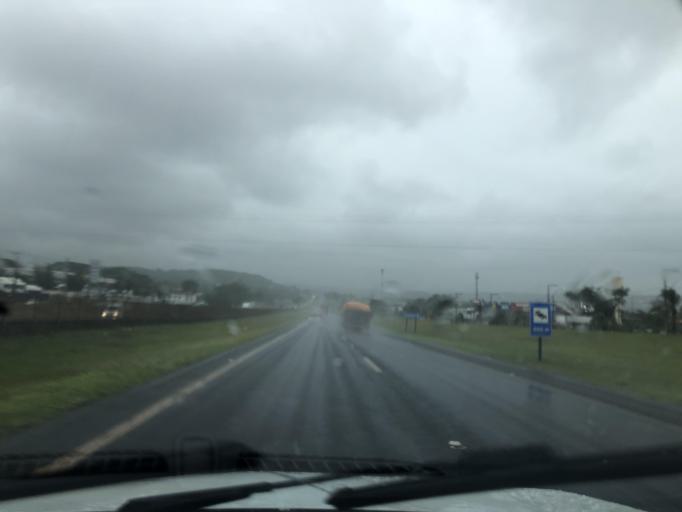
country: BR
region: Sao Paulo
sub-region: Ribeirao Preto
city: Ribeirao Preto
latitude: -21.2148
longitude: -47.7589
